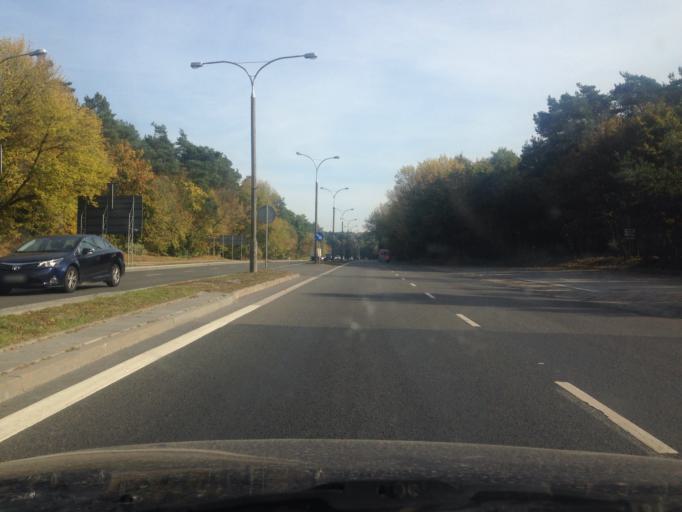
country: PL
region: Kujawsko-Pomorskie
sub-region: Wloclawek
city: Wloclawek
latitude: 52.6365
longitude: 19.0814
